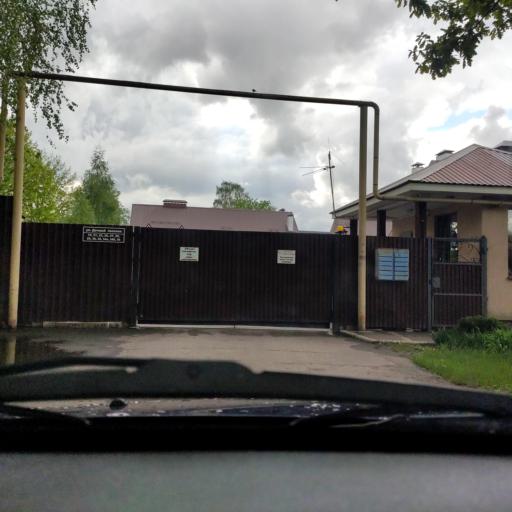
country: RU
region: Voronezj
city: Podgornoye
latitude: 51.7440
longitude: 39.1722
